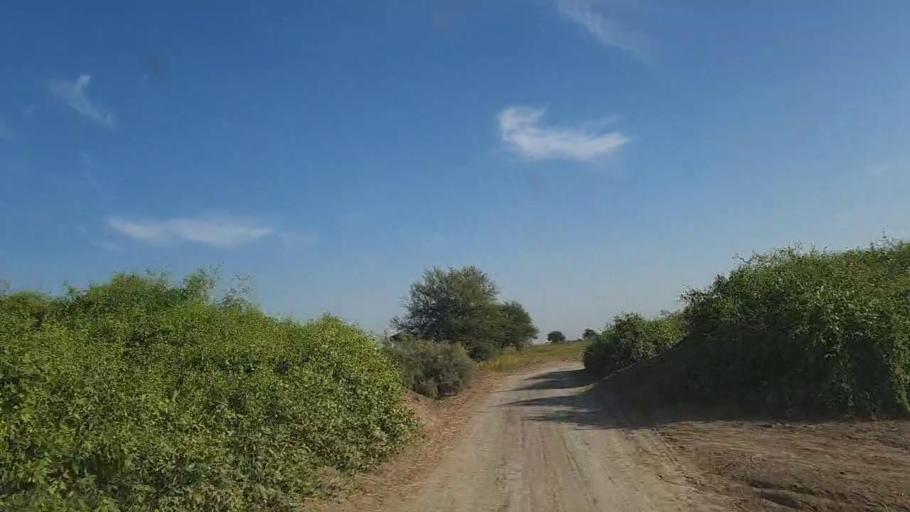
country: PK
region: Sindh
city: Mirpur Batoro
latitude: 24.7570
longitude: 68.3643
